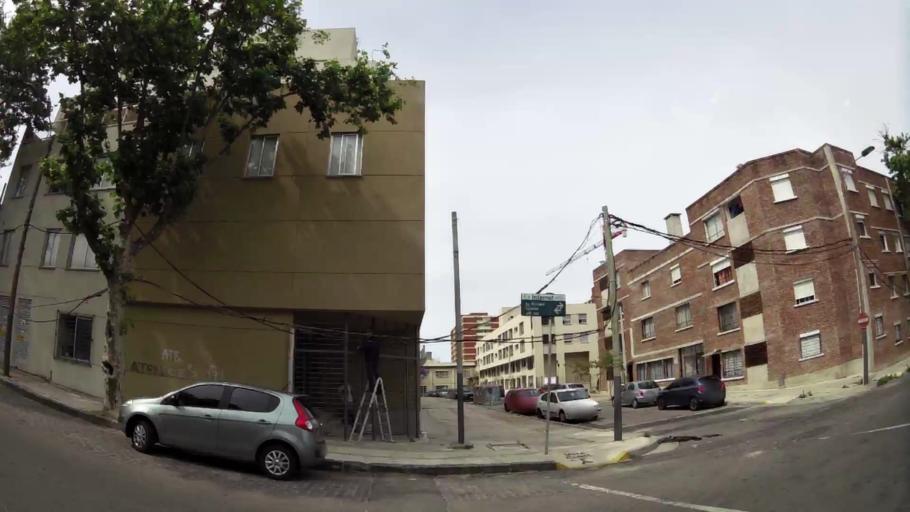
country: UY
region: Montevideo
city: Montevideo
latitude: -34.9118
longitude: -56.1883
